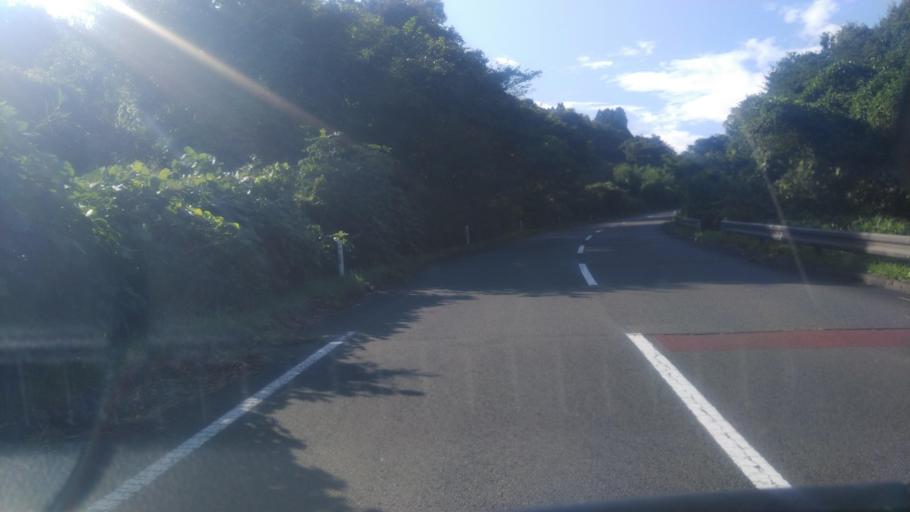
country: JP
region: Miyagi
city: Okawara
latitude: 38.0984
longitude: 140.6995
